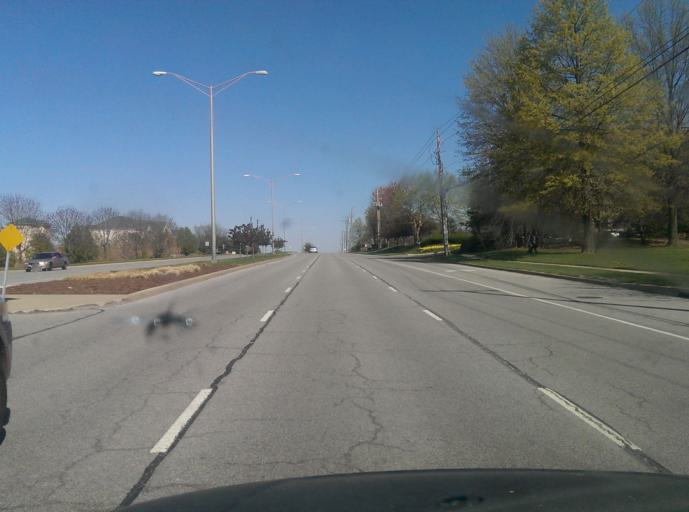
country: US
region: Kansas
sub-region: Johnson County
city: Leawood
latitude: 38.9275
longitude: -94.6560
